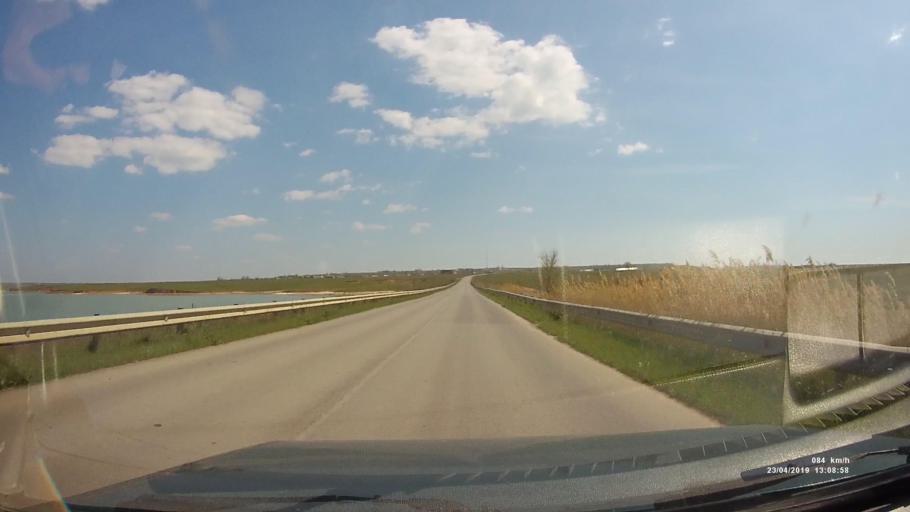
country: RU
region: Kalmykiya
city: Yashalta
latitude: 46.5788
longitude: 42.7831
